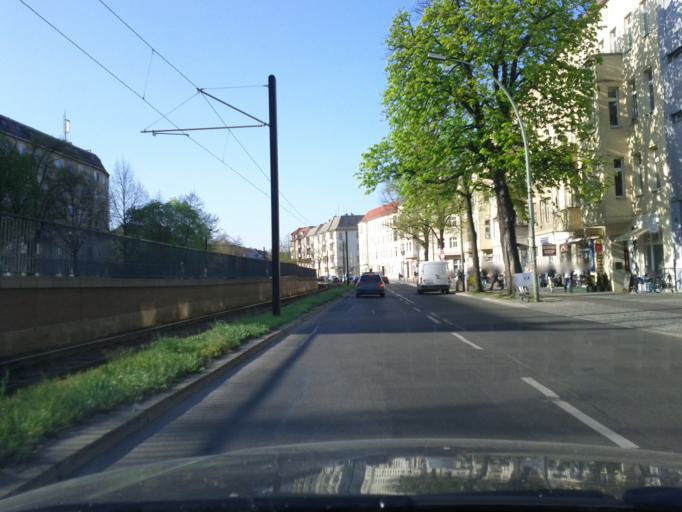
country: DE
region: Berlin
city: Pankow
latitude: 52.5562
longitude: 13.4146
